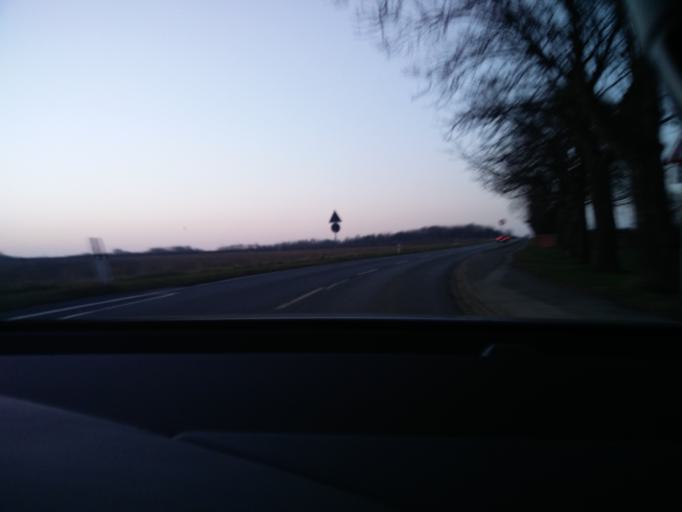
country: DE
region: Lower Saxony
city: Laatzen
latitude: 52.3301
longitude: 9.8456
